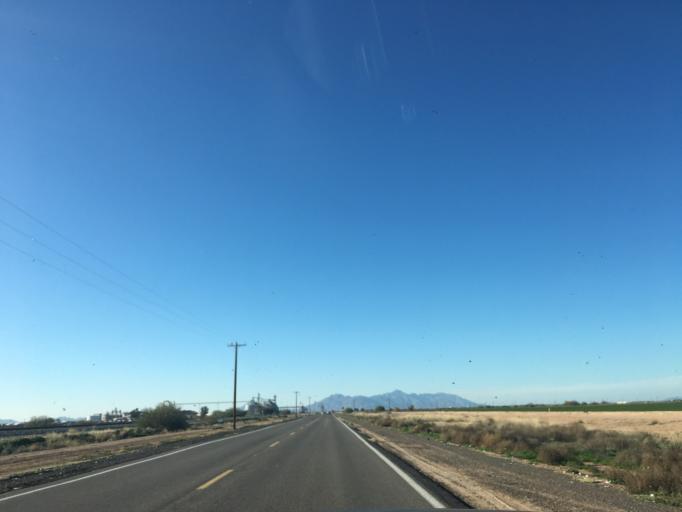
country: US
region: Arizona
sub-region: Pinal County
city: Maricopa
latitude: 33.0077
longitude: -111.9685
